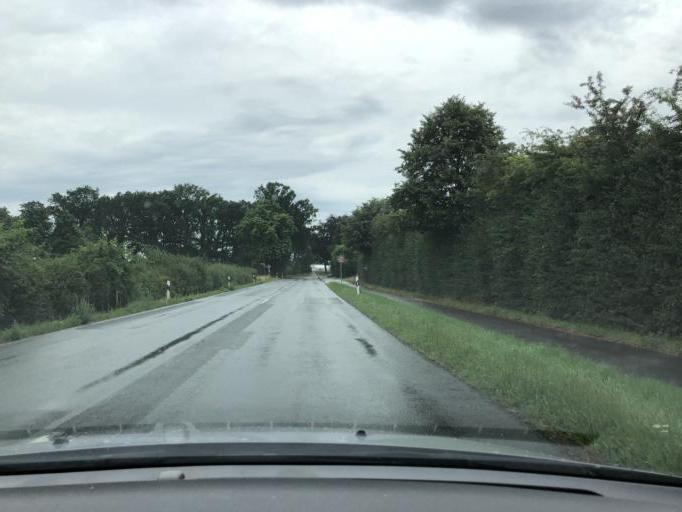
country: DE
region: North Rhine-Westphalia
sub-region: Regierungsbezirk Dusseldorf
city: Schermbeck
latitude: 51.7039
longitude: 6.8757
